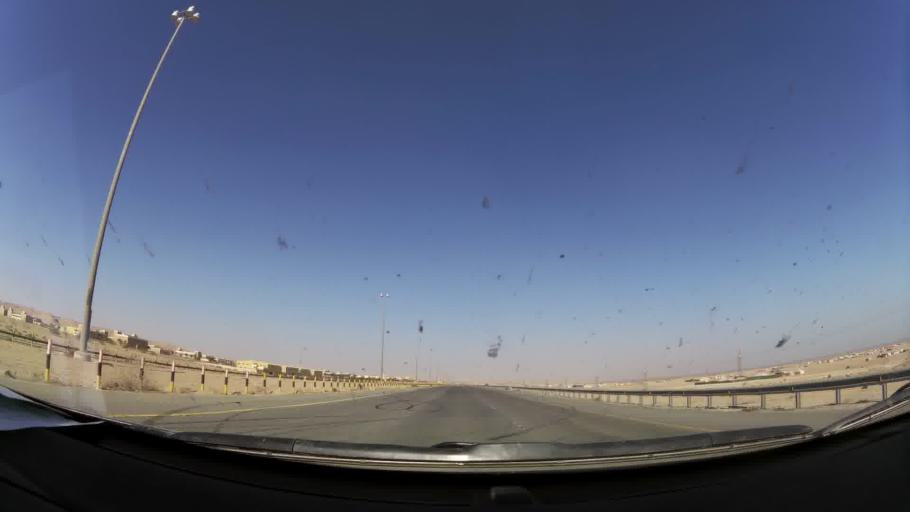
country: KW
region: Muhafazat al Jahra'
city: Al Jahra'
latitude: 29.4533
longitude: 47.7582
